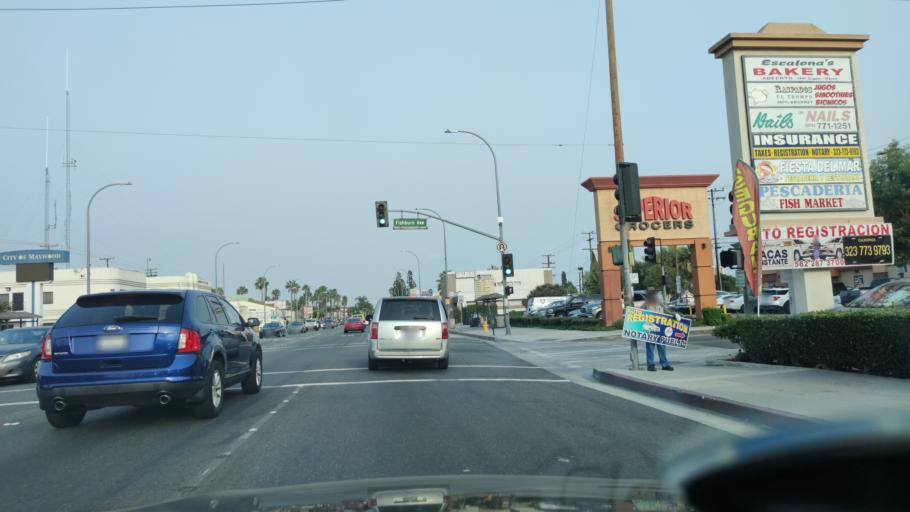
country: US
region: California
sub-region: Los Angeles County
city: Maywood
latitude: 33.9876
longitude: -118.1903
